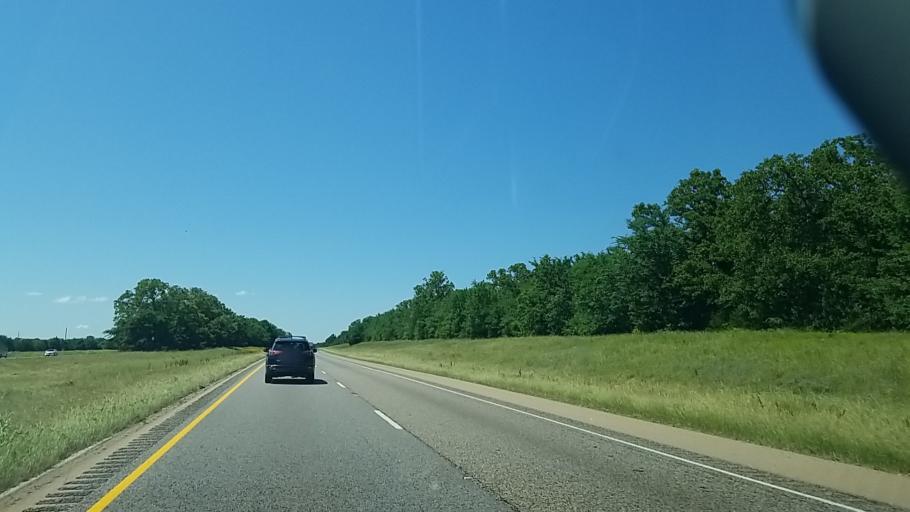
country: US
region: Texas
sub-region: Leon County
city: Buffalo
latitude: 31.5430
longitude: -96.1243
